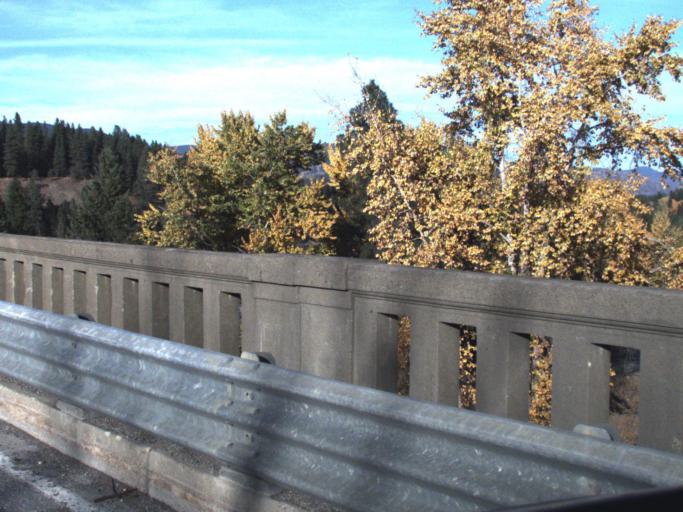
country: CA
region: British Columbia
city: Rossland
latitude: 48.9202
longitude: -117.7763
